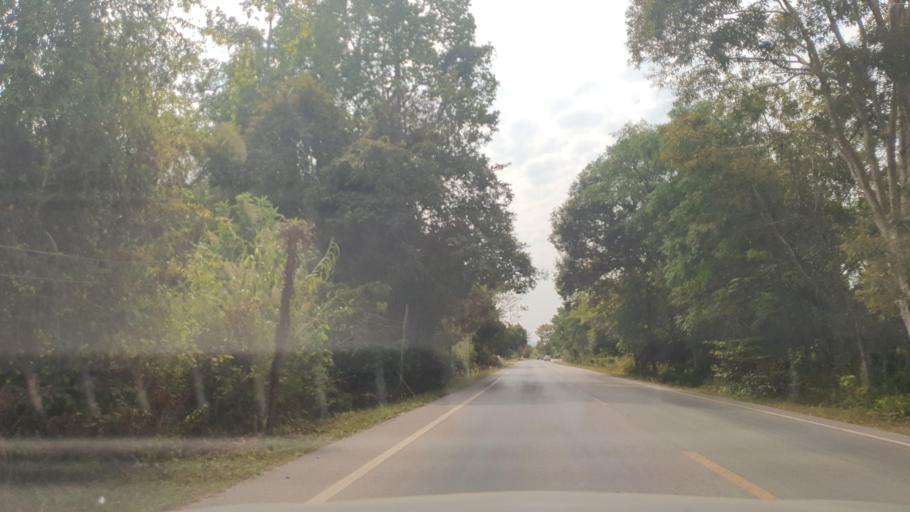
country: TH
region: Changwat Bueng Kan
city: Bung Khla
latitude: 18.2868
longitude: 103.8854
